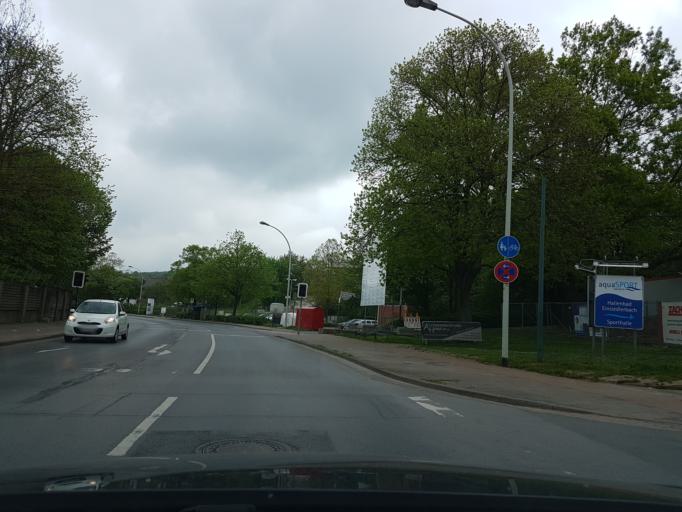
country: DE
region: Lower Saxony
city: Hameln
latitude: 52.1150
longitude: 9.3689
